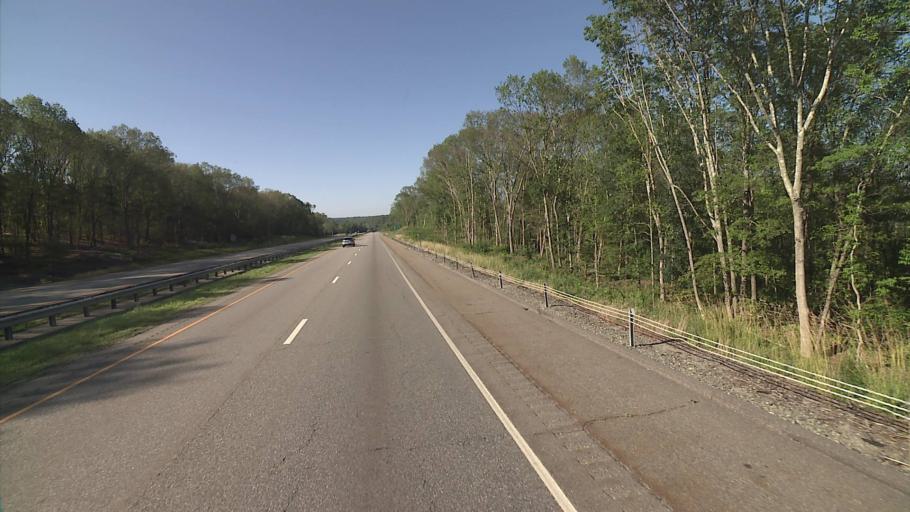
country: US
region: Connecticut
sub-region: New London County
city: Jewett City
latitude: 41.6201
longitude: -71.9447
